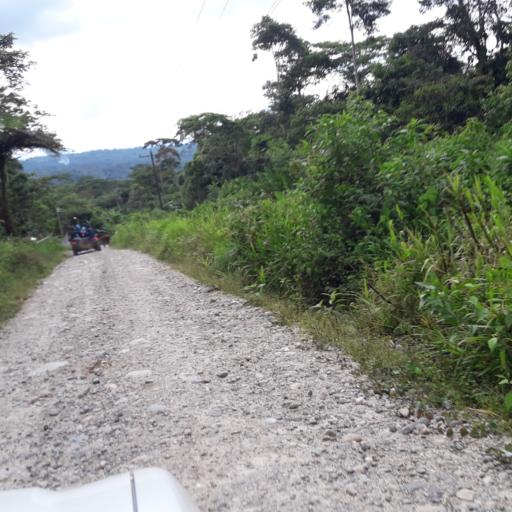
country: EC
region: Napo
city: Archidona
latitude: -0.9433
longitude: -77.8856
